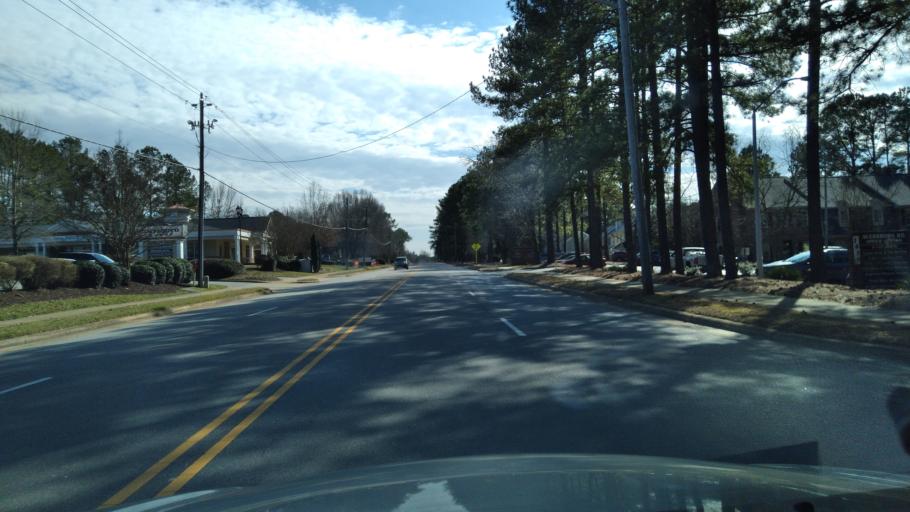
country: US
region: North Carolina
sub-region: Wake County
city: Garner
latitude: 35.6948
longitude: -78.6167
